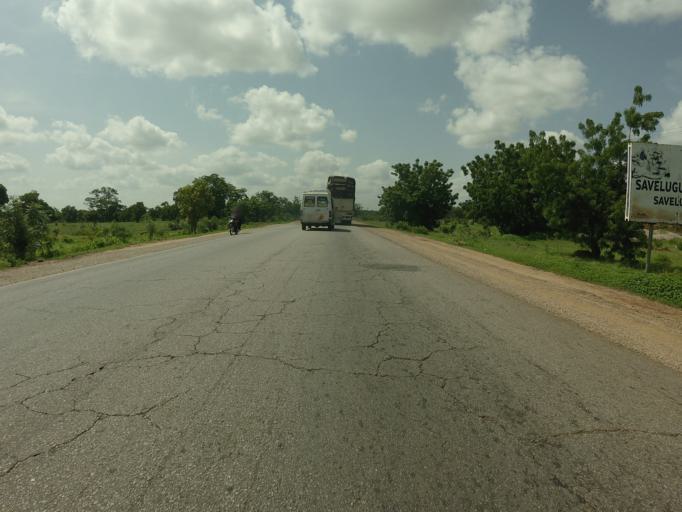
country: GH
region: Northern
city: Savelugu
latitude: 9.5619
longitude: -0.8362
